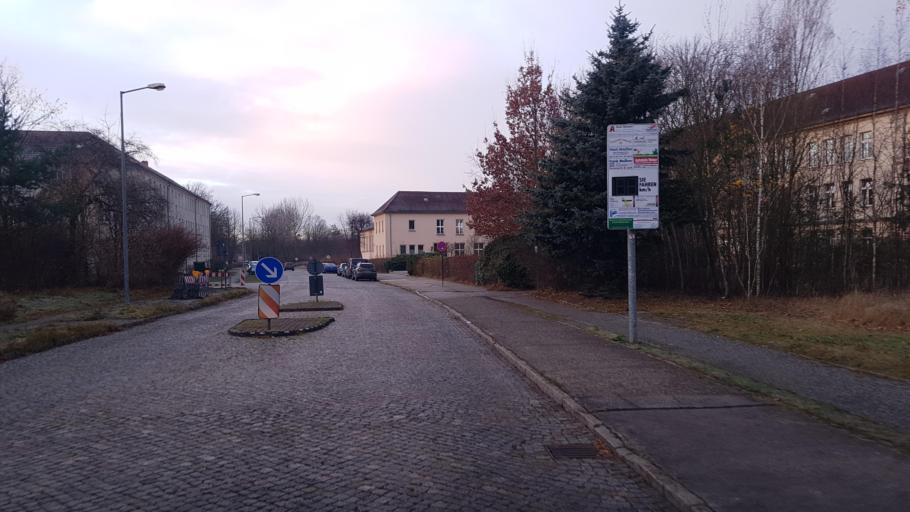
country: DE
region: Brandenburg
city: Lauchhammer
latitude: 51.4989
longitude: 13.7461
